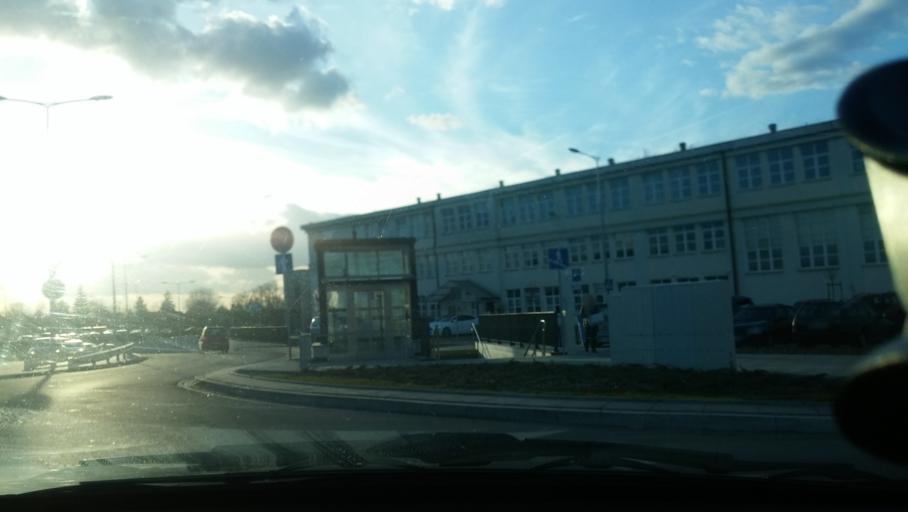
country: PL
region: Masovian Voivodeship
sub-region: Warszawa
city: Wawer
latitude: 52.2056
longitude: 21.1710
